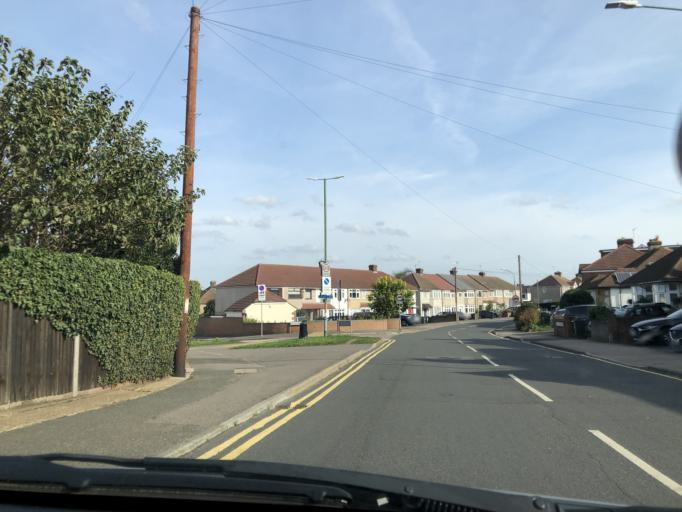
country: GB
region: England
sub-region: Greater London
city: Bexley
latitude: 51.4444
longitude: 0.1826
